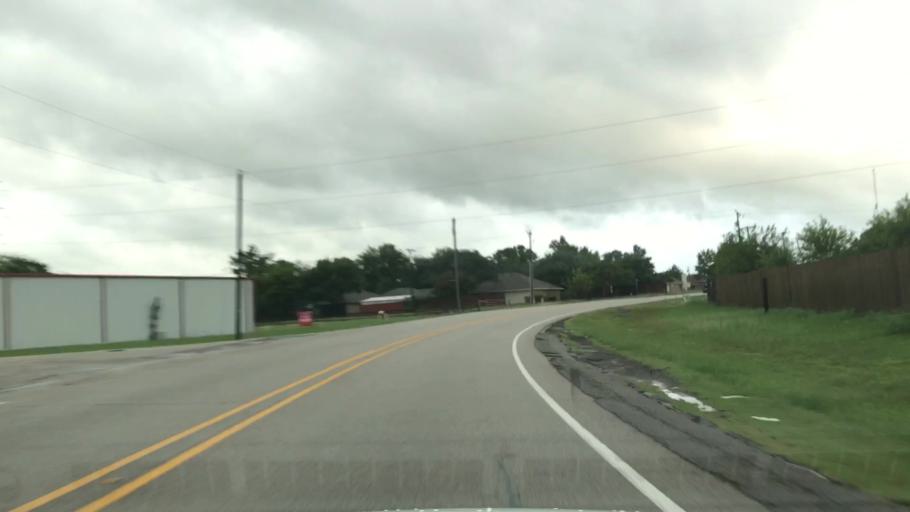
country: US
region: Texas
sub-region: Collin County
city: Wylie
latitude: 33.0266
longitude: -96.5390
